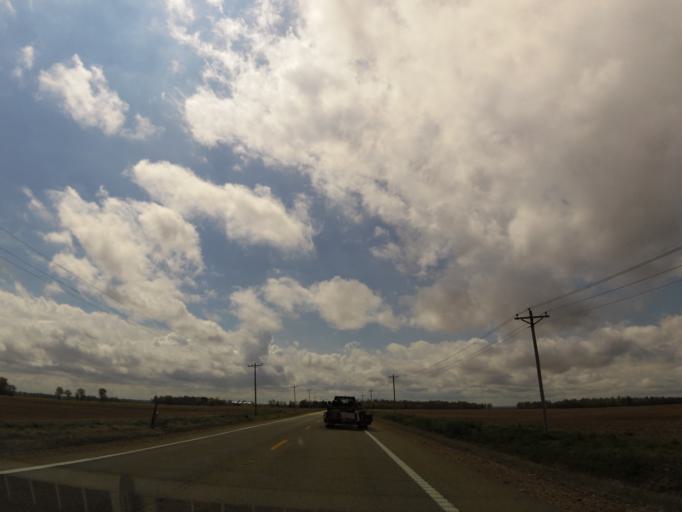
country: US
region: Arkansas
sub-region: Clay County
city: Corning
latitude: 36.3477
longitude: -90.5251
